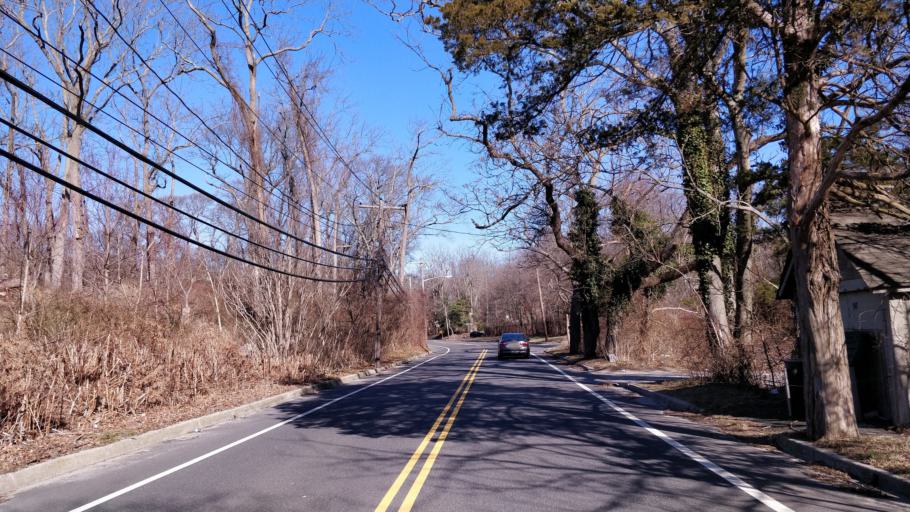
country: US
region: New York
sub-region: Suffolk County
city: Setauket-East Setauket
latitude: 40.9239
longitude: -73.1128
